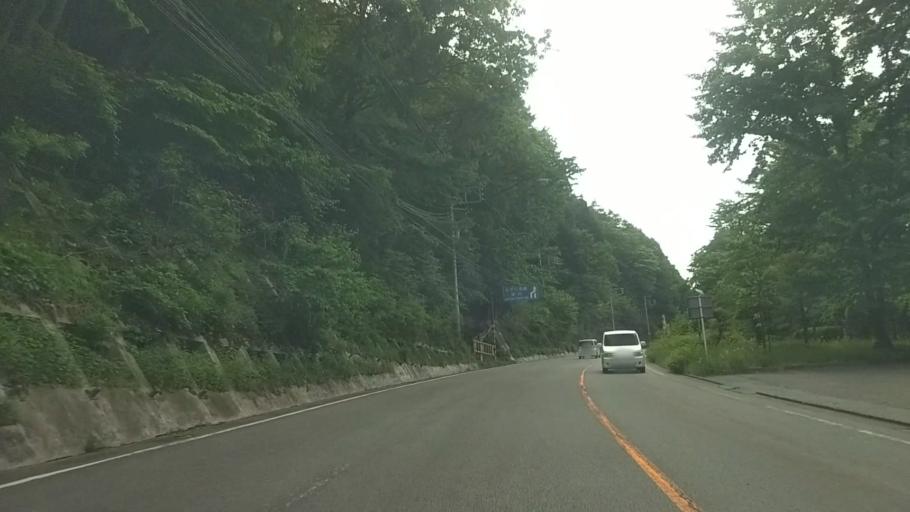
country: JP
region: Yamanashi
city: Fujikawaguchiko
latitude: 35.5266
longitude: 138.6219
